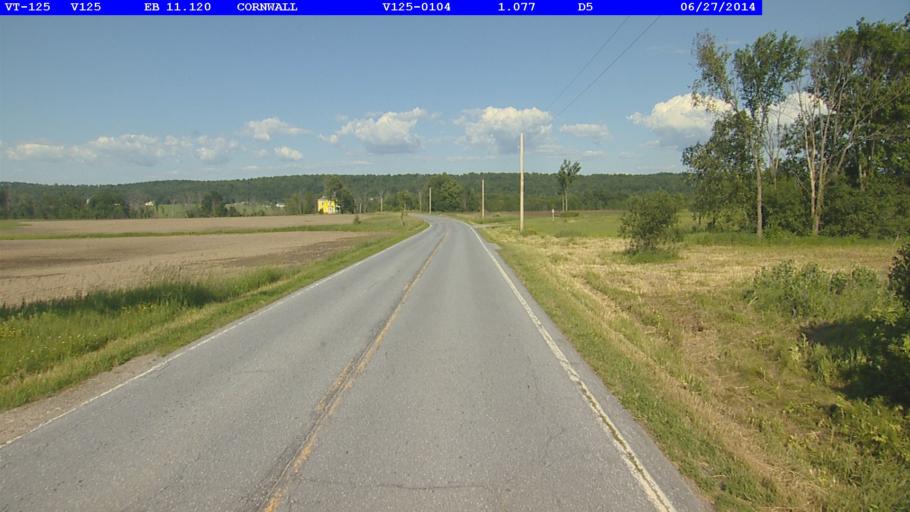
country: US
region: Vermont
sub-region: Addison County
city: Middlebury (village)
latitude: 43.9917
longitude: -73.2417
